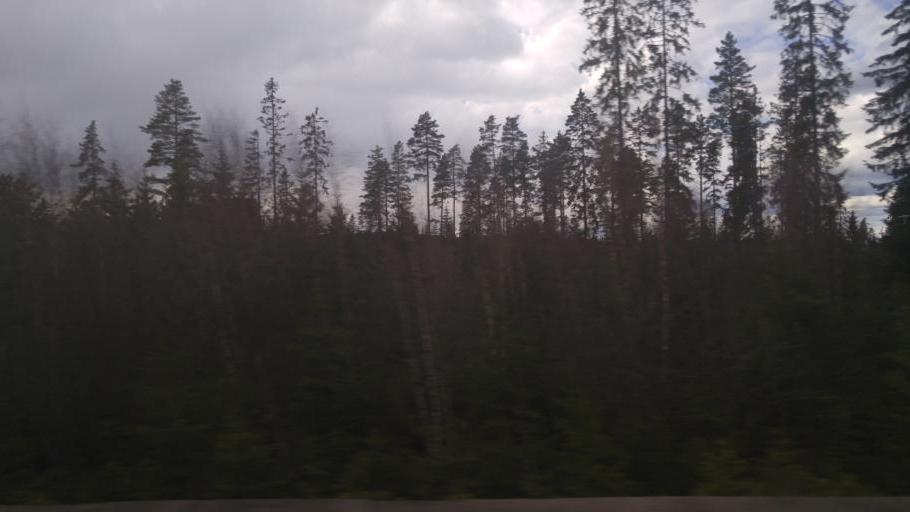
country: NO
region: Akershus
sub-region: Eidsvoll
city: Raholt
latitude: 60.2574
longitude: 11.1332
